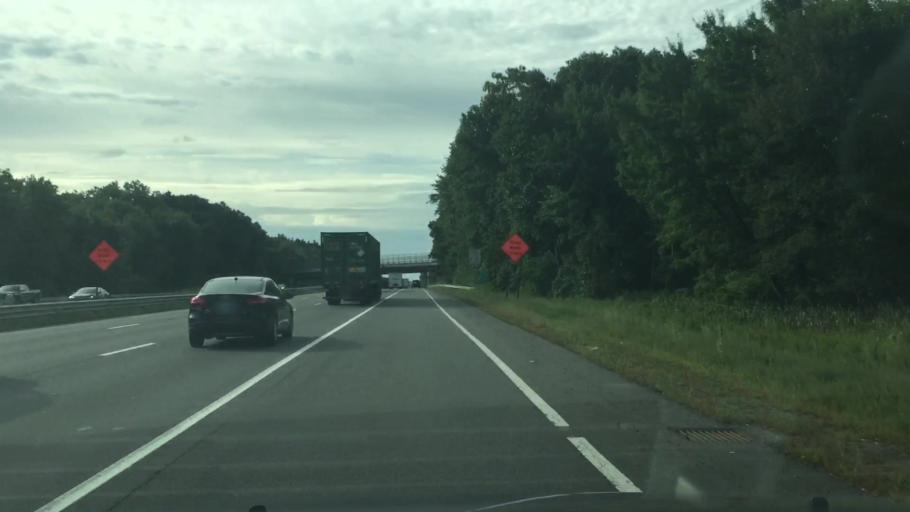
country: US
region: Massachusetts
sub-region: Essex County
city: Methuen
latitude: 42.6834
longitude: -71.2034
